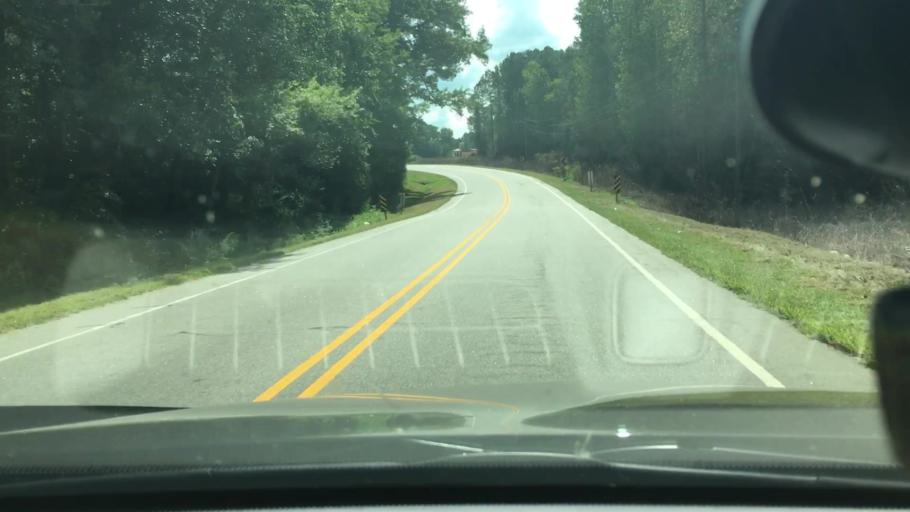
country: US
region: North Carolina
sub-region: Edgecombe County
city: Pinetops
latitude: 35.7828
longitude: -77.6160
